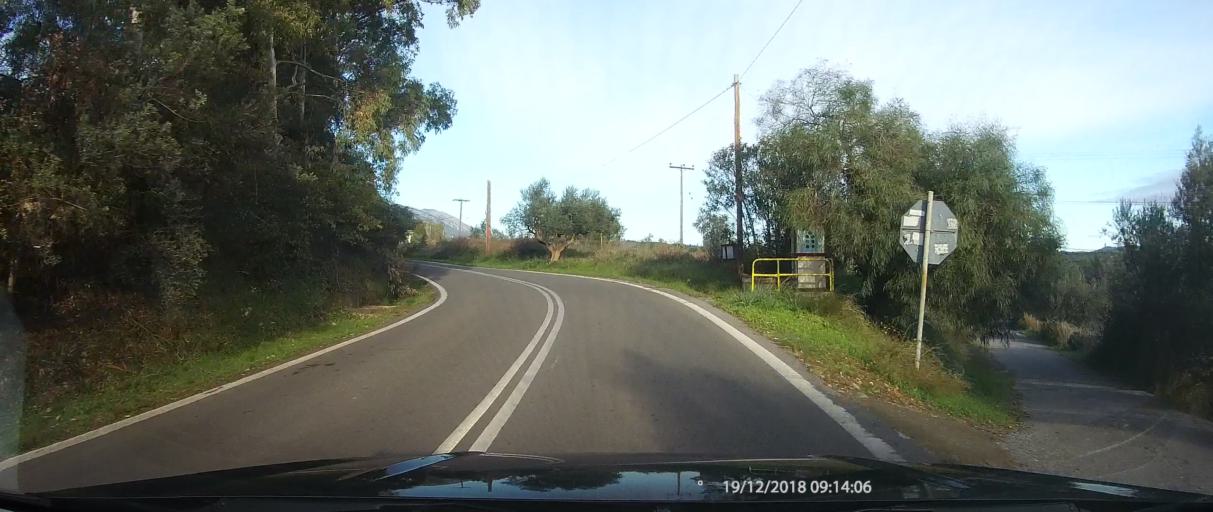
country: GR
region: Peloponnese
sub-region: Nomos Lakonias
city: Magoula
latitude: 37.0847
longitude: 22.3922
